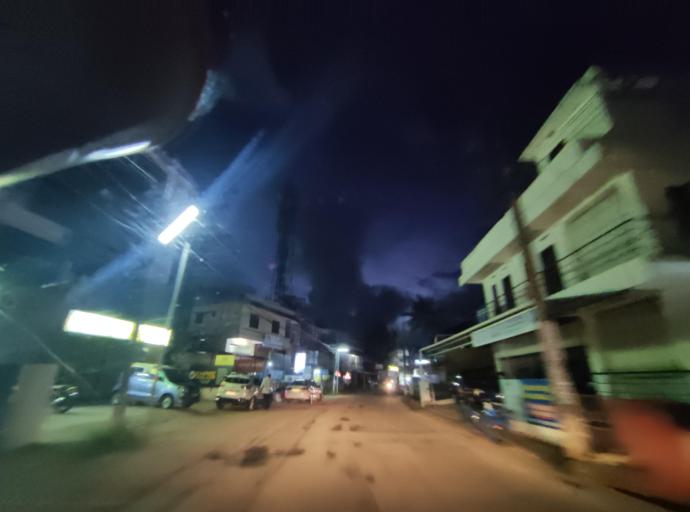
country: IN
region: Kerala
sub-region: Thiruvananthapuram
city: Nedumangad
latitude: 8.5629
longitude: 76.9554
